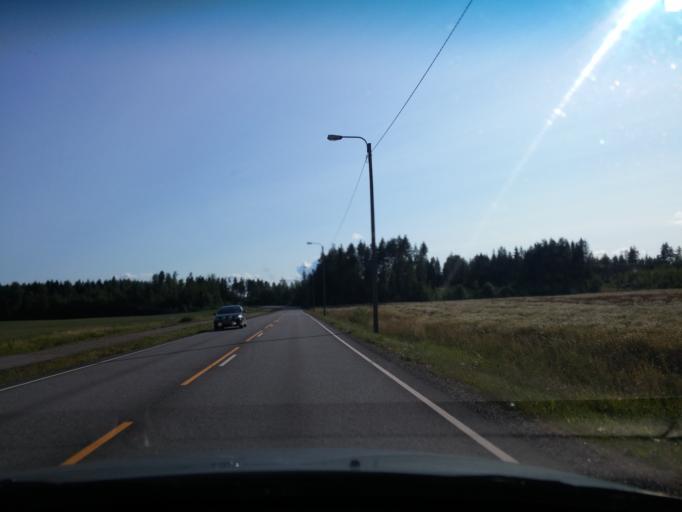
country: FI
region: Uusimaa
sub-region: Porvoo
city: Askola
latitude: 60.5074
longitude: 25.5699
